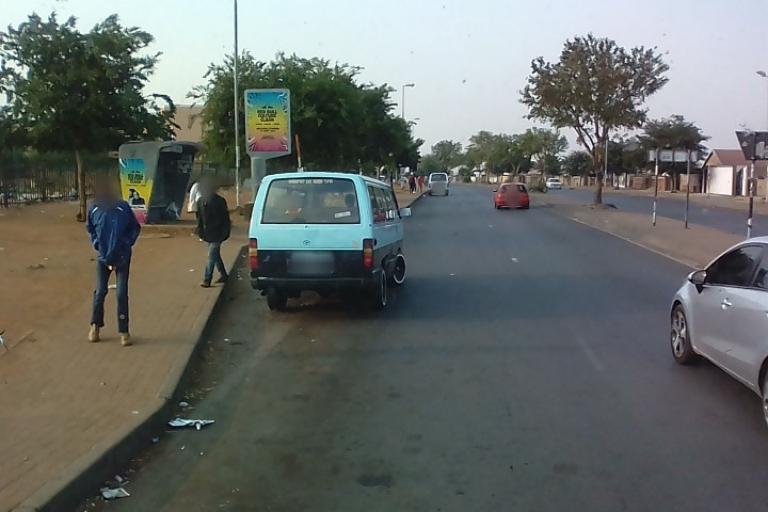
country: ZA
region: Gauteng
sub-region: City of Johannesburg Metropolitan Municipality
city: Soweto
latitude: -26.2491
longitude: 27.8541
